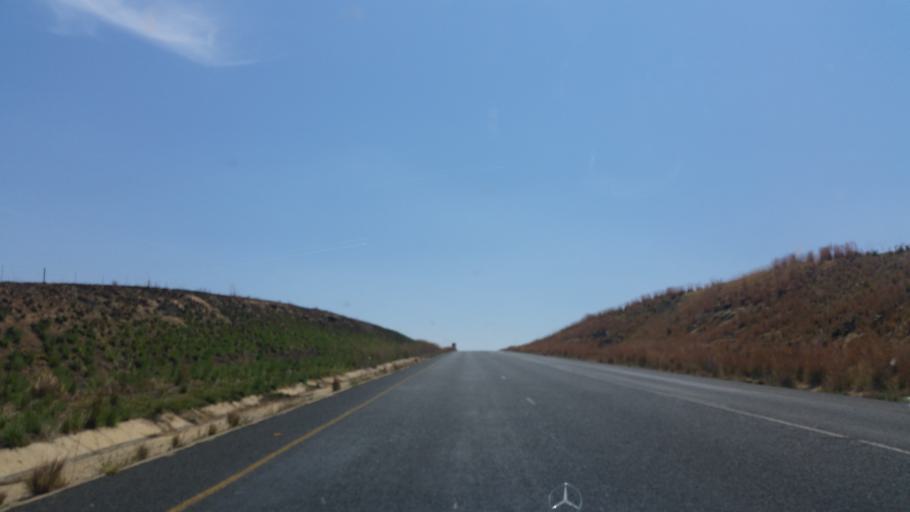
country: ZA
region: Orange Free State
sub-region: Thabo Mofutsanyana District Municipality
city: Phuthaditjhaba
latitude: -28.1729
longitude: 28.6842
